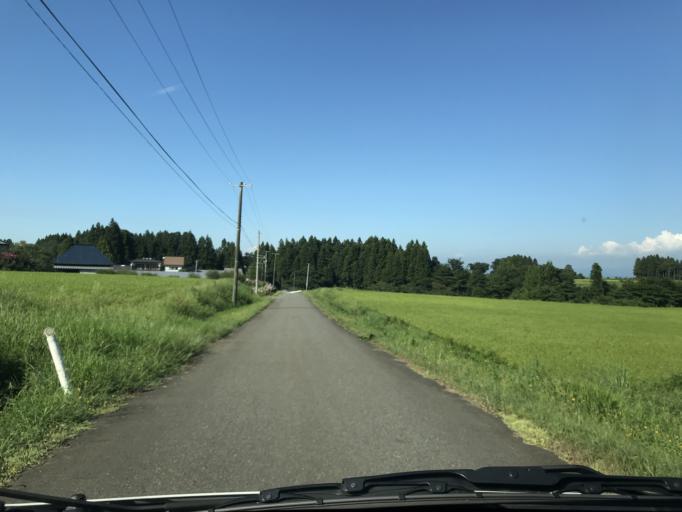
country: JP
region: Iwate
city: Mizusawa
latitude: 39.0694
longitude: 141.0455
